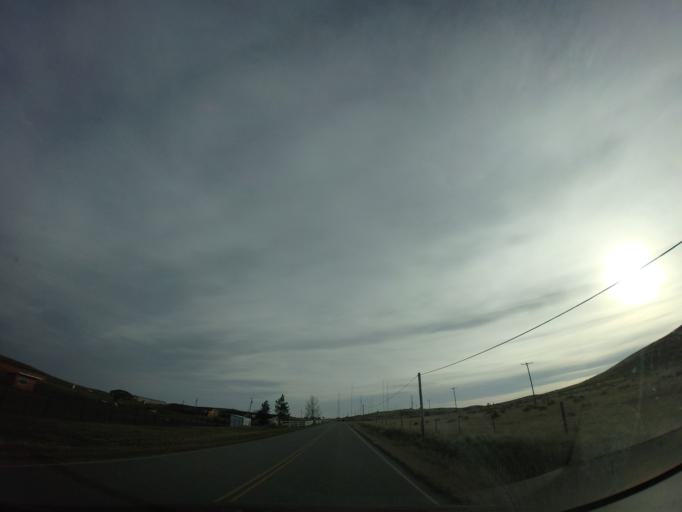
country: US
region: Montana
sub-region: Yellowstone County
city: Billings
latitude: 45.7756
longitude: -108.4622
